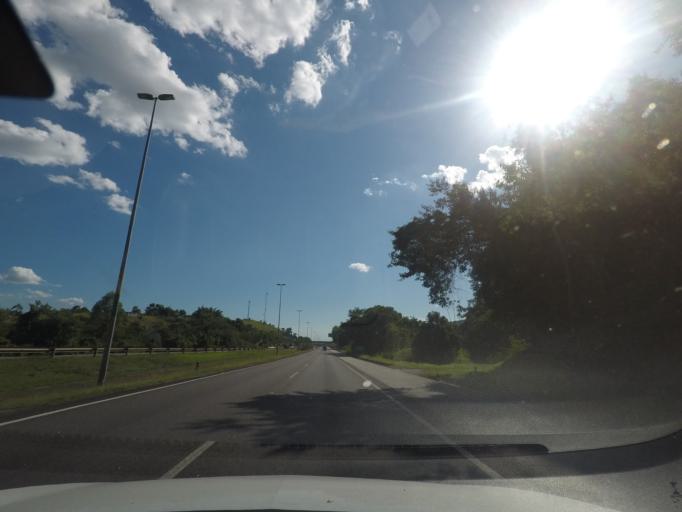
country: BR
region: Rio de Janeiro
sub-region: Guapimirim
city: Guapimirim
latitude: -22.6082
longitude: -43.0299
